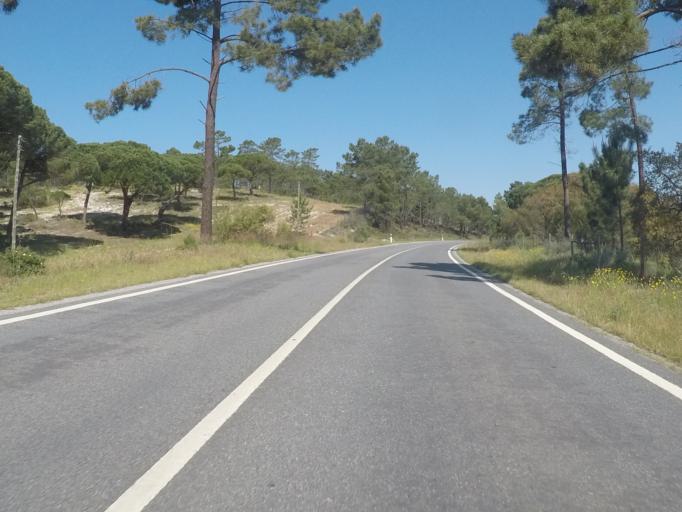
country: PT
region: Setubal
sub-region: Grandola
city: Grandola
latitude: 38.3020
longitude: -8.7341
